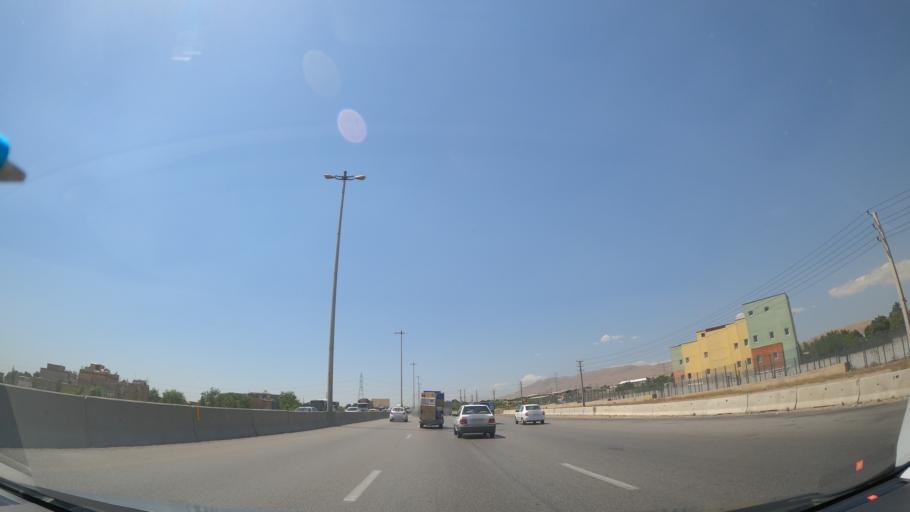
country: IR
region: Alborz
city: Karaj
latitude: 35.8678
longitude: 50.9006
